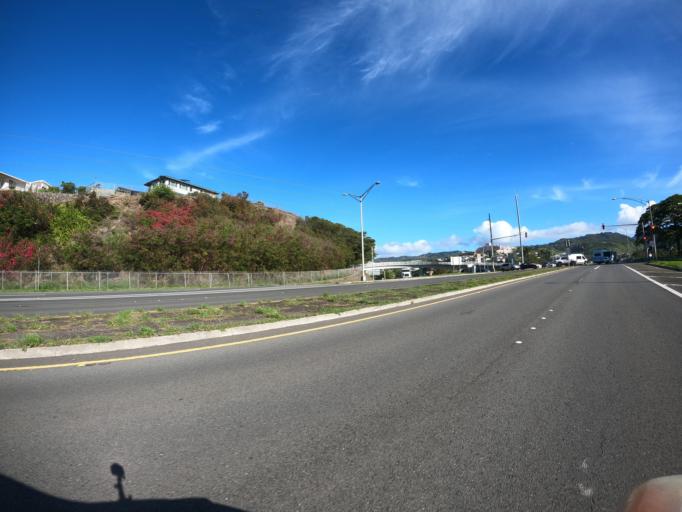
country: US
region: Hawaii
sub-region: Honolulu County
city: Halawa Heights
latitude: 21.3484
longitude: -157.8967
